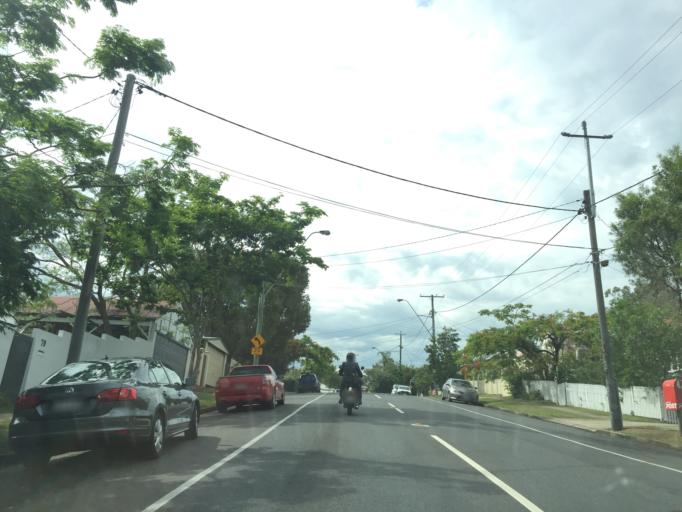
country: AU
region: Queensland
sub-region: Brisbane
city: Milton
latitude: -27.4548
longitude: 152.9820
